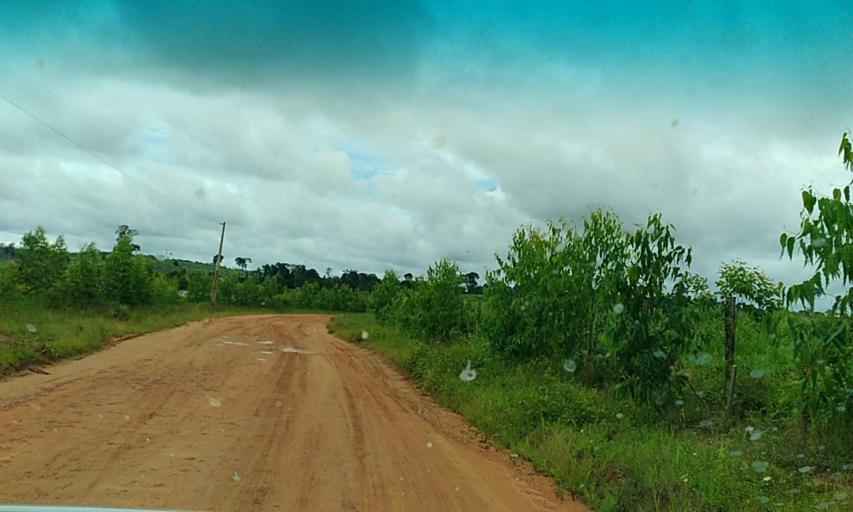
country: BR
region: Para
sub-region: Altamira
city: Altamira
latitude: -3.0574
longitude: -51.7232
